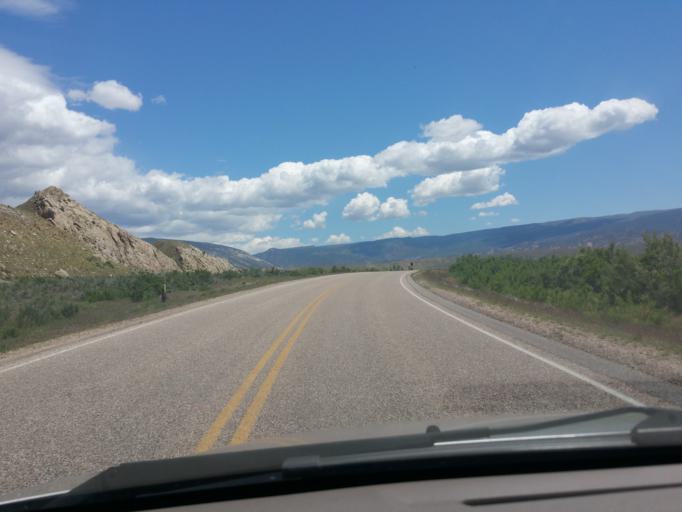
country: US
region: Utah
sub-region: Uintah County
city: Naples
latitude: 40.4387
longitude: -109.3129
